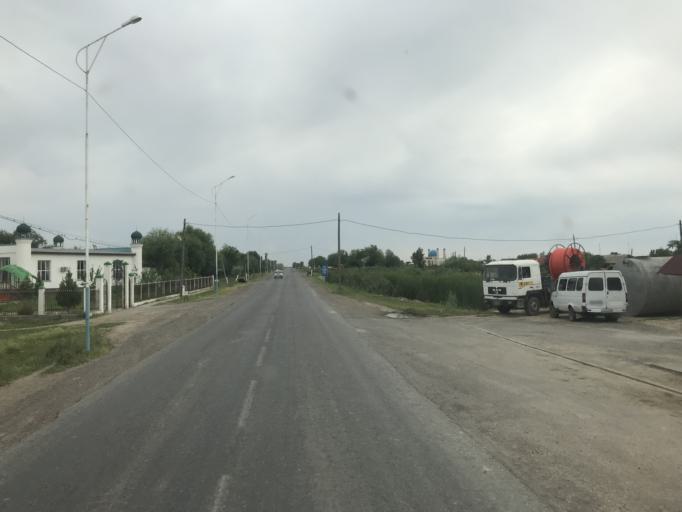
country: KZ
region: Ongtustik Qazaqstan
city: Asykata
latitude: 40.9333
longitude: 68.4089
